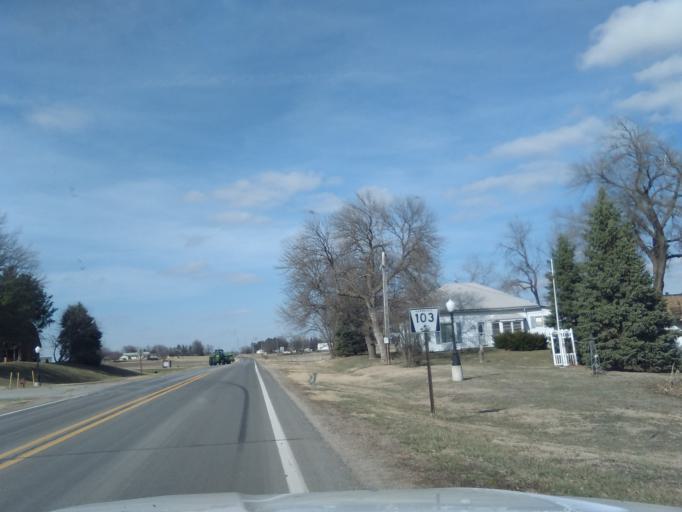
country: US
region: Nebraska
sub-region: Gage County
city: Beatrice
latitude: 40.1120
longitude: -96.9350
